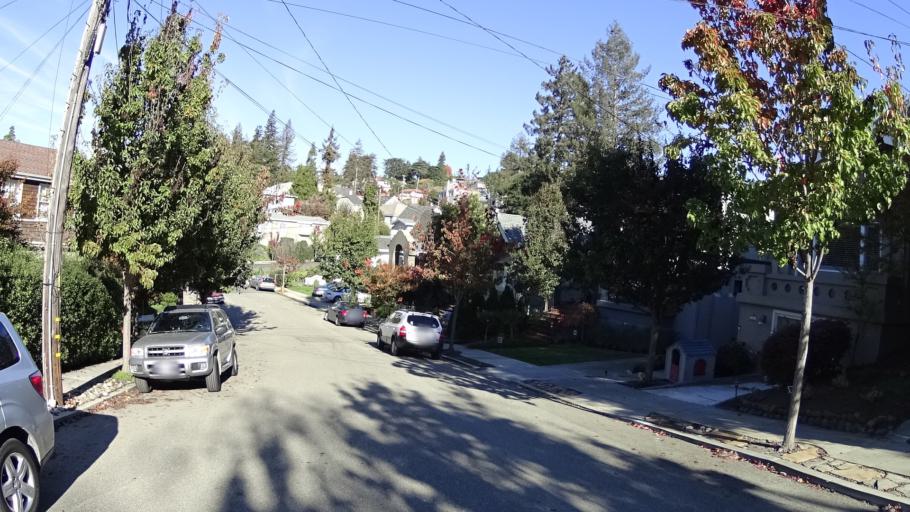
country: US
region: California
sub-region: Alameda County
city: Piedmont
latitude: 37.8175
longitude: -122.2349
